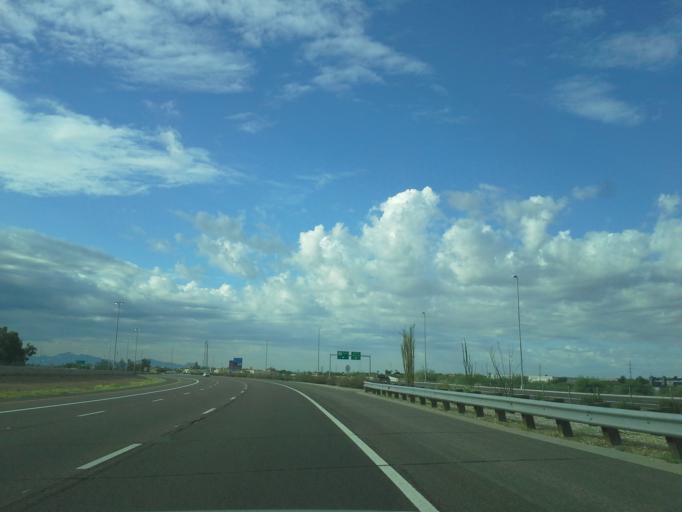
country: US
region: Arizona
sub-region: Maricopa County
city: Sun City
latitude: 33.6631
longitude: -112.2315
